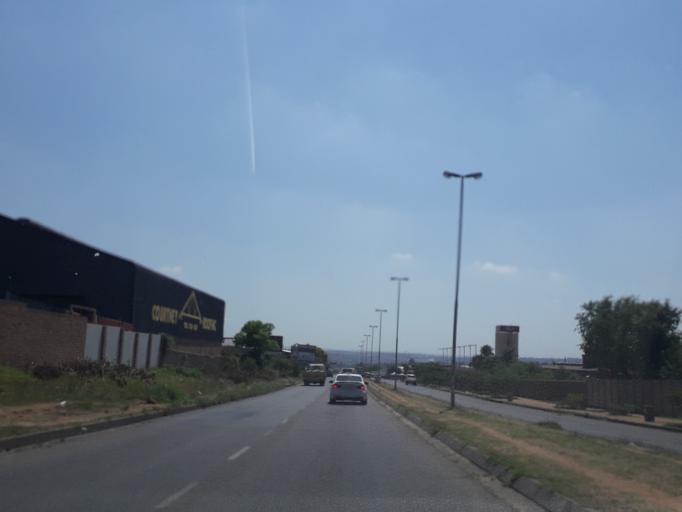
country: ZA
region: Gauteng
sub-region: West Rand District Municipality
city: Muldersdriseloop
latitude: -26.0279
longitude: 27.9473
